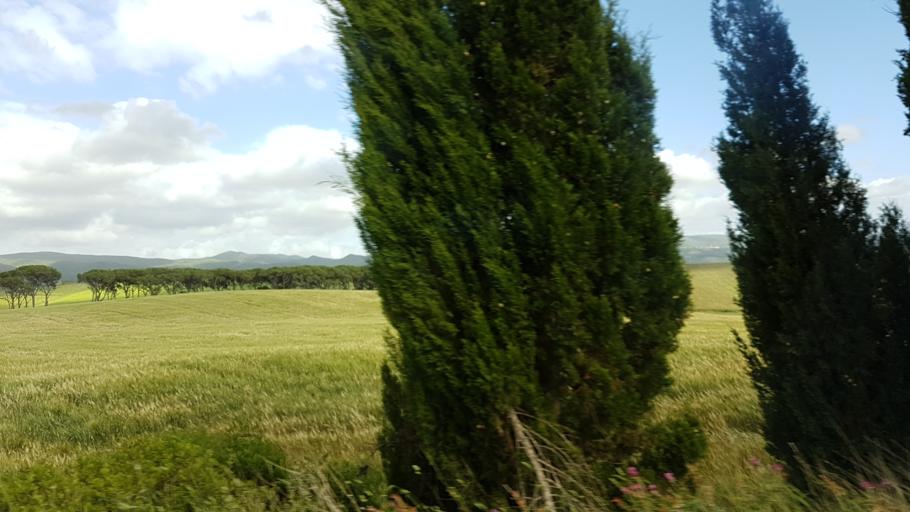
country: IT
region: Tuscany
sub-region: Province of Pisa
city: Santa Luce
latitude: 43.4581
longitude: 10.5273
